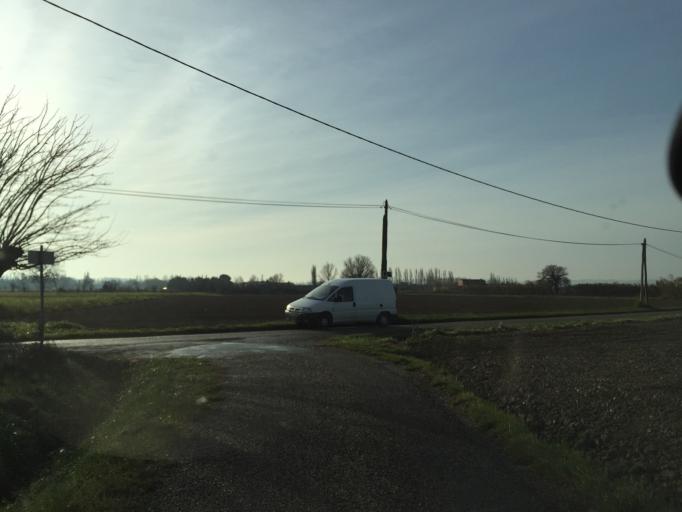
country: FR
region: Provence-Alpes-Cote d'Azur
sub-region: Departement du Vaucluse
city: Caderousse
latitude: 44.1301
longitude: 4.7645
